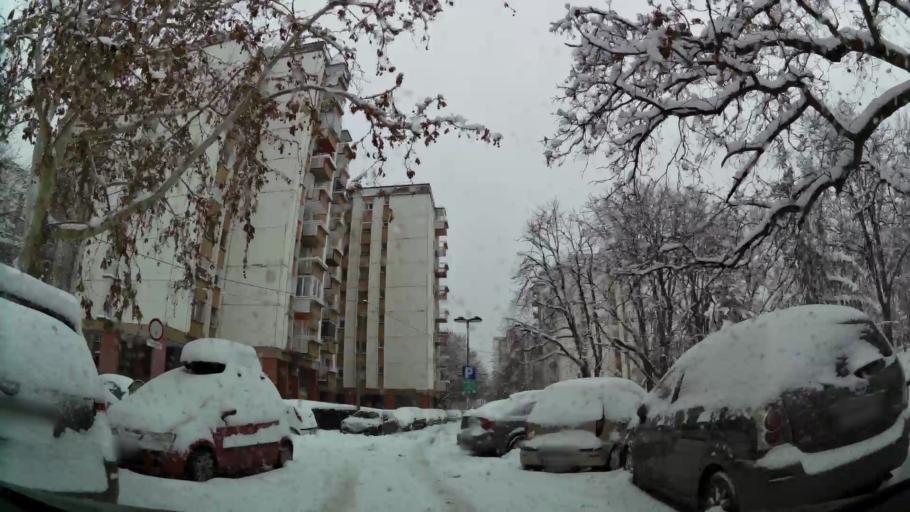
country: RS
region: Central Serbia
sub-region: Belgrade
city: Stari Grad
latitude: 44.8248
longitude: 20.4636
